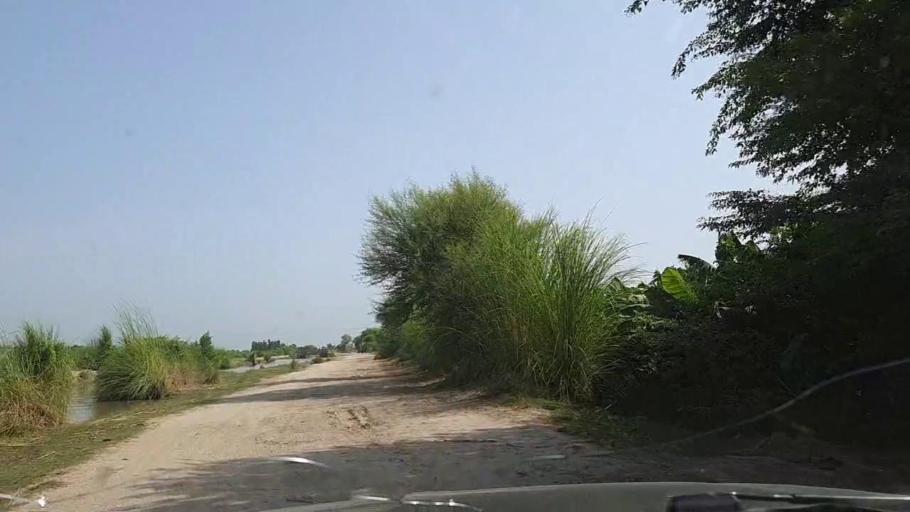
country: PK
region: Sindh
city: Ghotki
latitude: 28.0561
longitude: 69.3795
